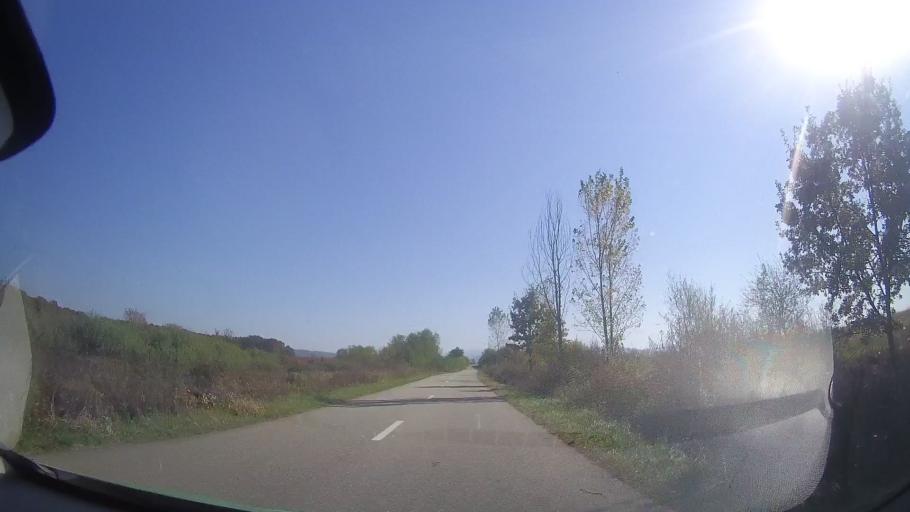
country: RO
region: Timis
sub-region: Comuna Traian Vuia
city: Traian Vuia
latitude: 45.7845
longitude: 22.0434
